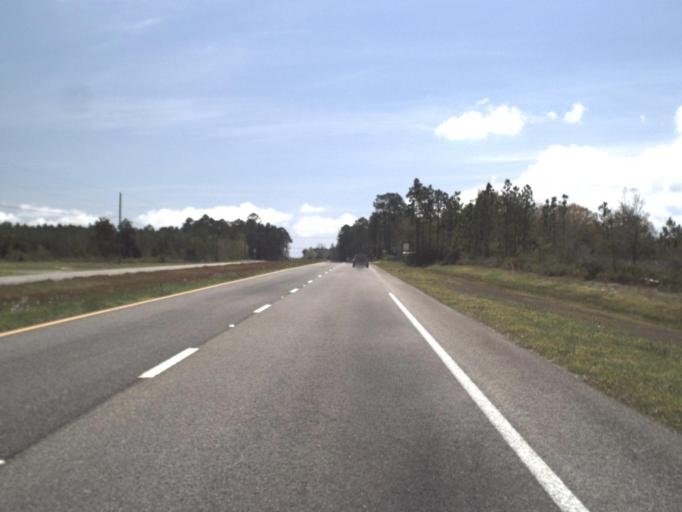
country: US
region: Florida
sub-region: Bay County
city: Laguna Beach
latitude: 30.3367
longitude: -85.8588
